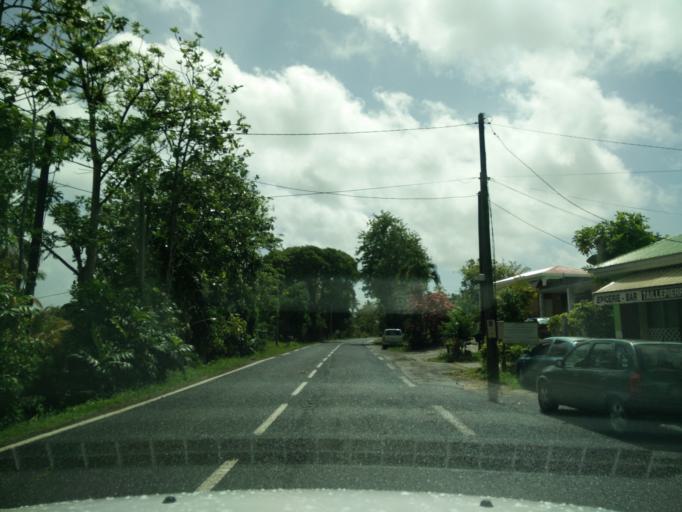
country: GP
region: Guadeloupe
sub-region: Guadeloupe
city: Grand-Bourg
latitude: 15.8965
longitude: -61.2944
